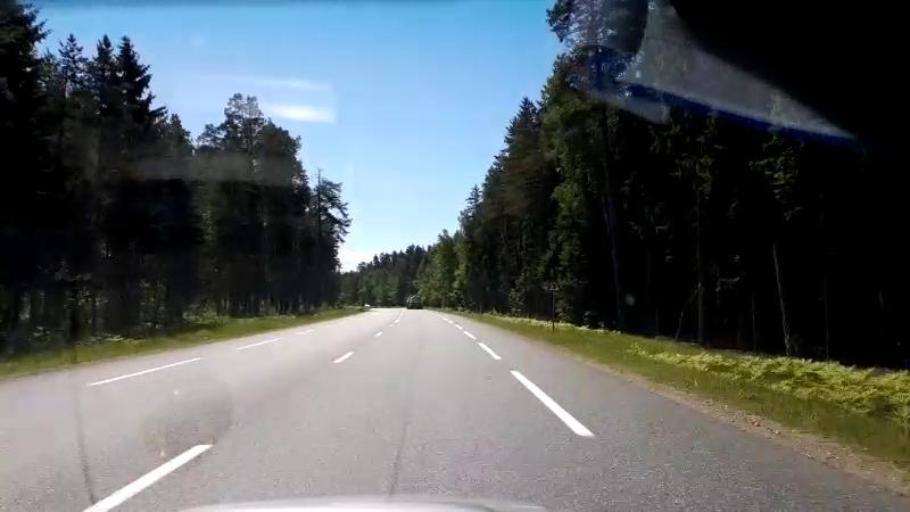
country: LV
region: Saulkrastu
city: Saulkrasti
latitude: 57.3991
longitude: 24.4281
